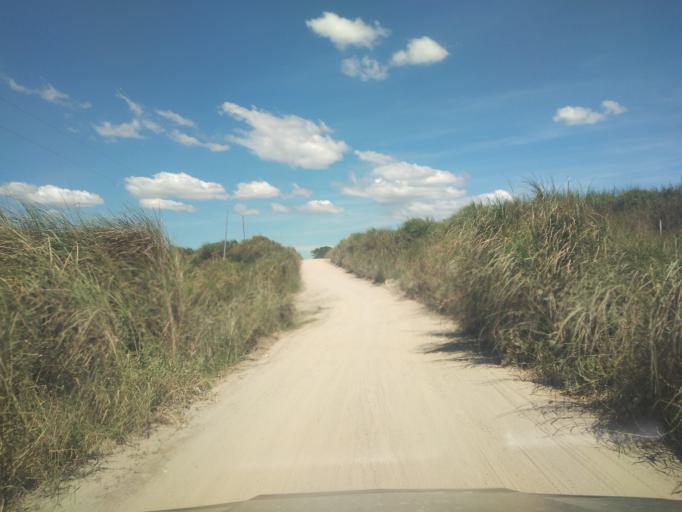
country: PH
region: Central Luzon
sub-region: Province of Pampanga
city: San Basilio
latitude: 15.0250
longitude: 120.6045
